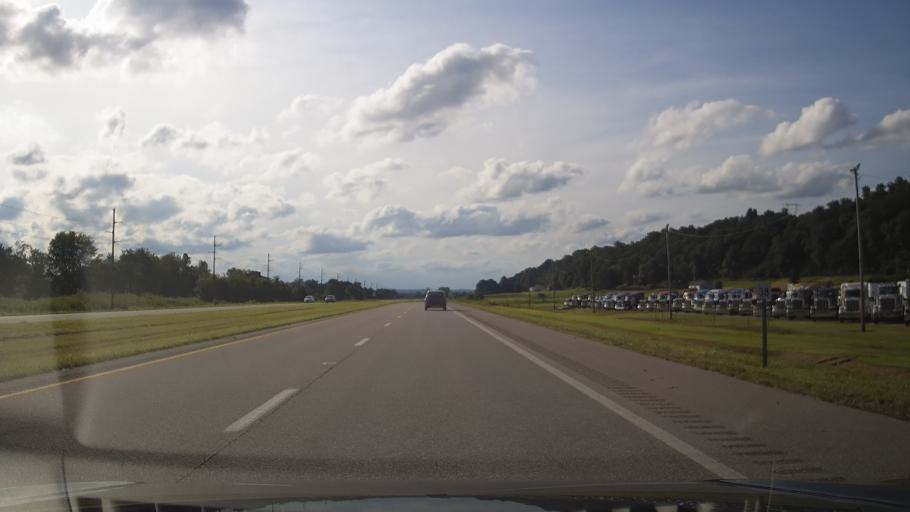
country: US
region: Kentucky
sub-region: Greenup County
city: Greenup
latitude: 38.5960
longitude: -82.8111
